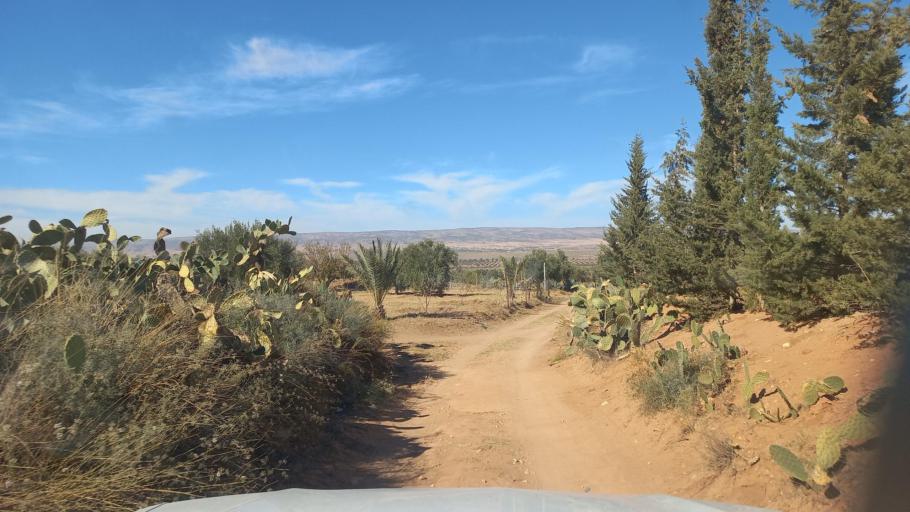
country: TN
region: Al Qasrayn
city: Kasserine
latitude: 35.2019
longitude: 8.9709
